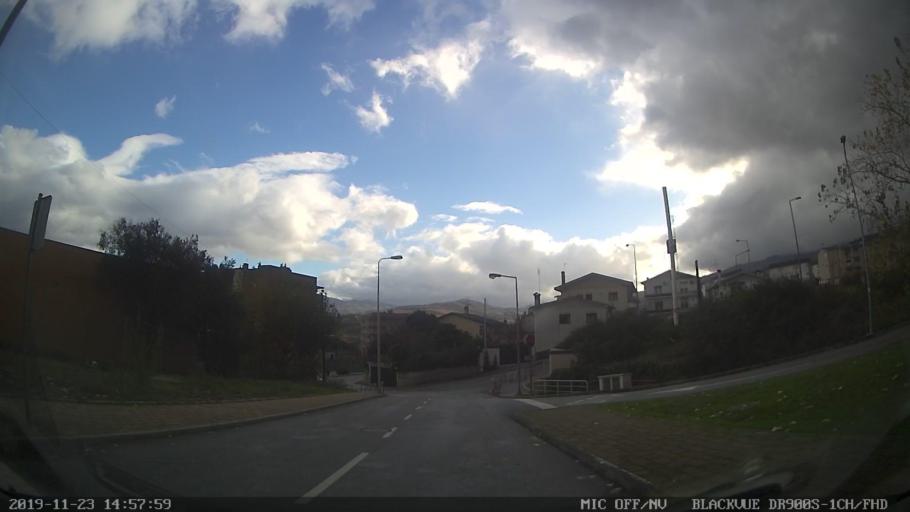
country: PT
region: Vila Real
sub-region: Peso da Regua
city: Godim
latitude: 41.1677
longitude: -7.8021
